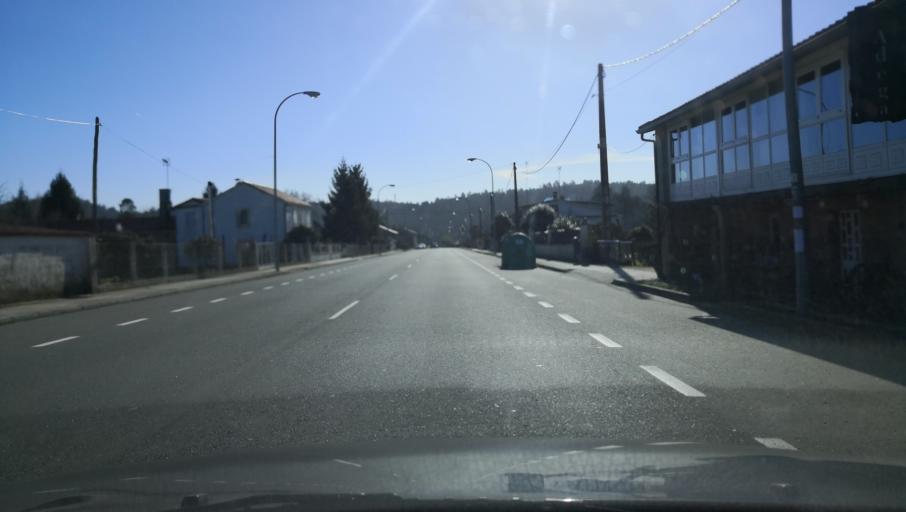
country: ES
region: Galicia
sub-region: Provincia de Pontevedra
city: Silleda
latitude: 42.7375
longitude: -8.3252
